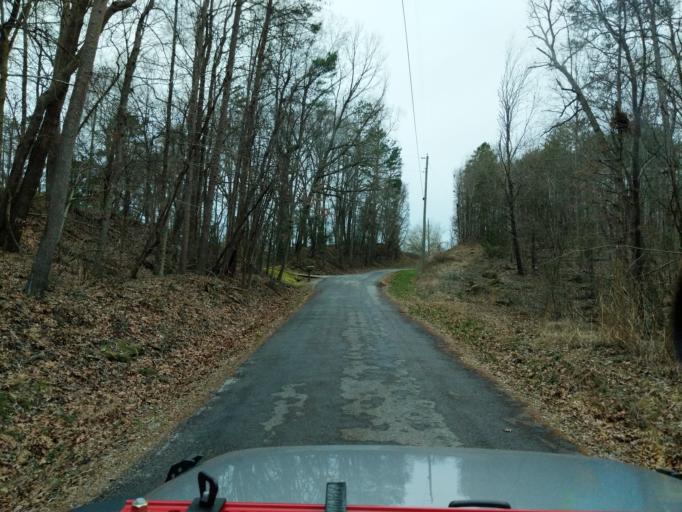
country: US
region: Georgia
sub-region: Franklin County
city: Gumlog
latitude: 34.4754
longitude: -83.0325
